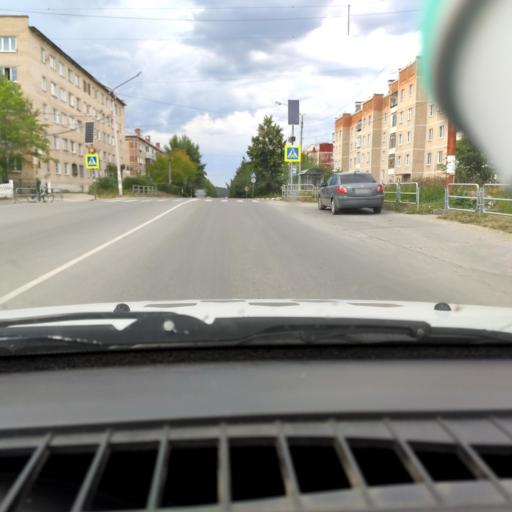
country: RU
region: Chelyabinsk
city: Miass
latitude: 55.0786
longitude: 60.0936
